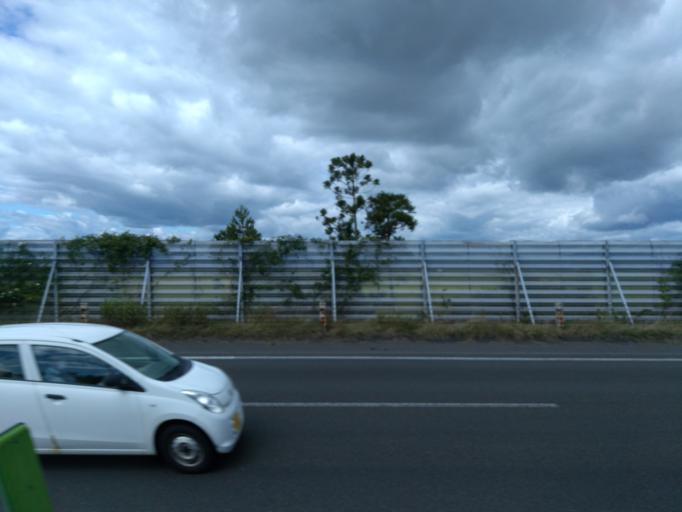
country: JP
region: Miyagi
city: Furukawa
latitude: 38.5876
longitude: 140.9306
